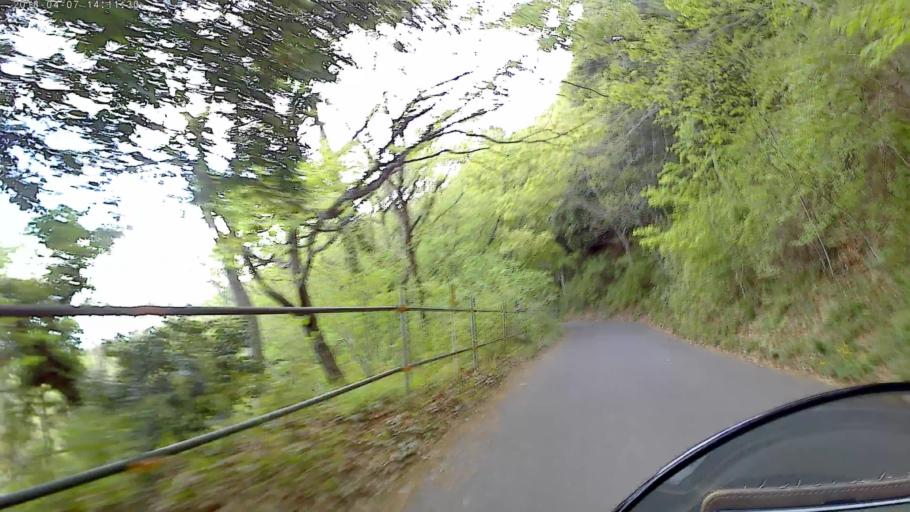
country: JP
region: Kanagawa
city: Hadano
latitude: 35.3709
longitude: 139.2435
